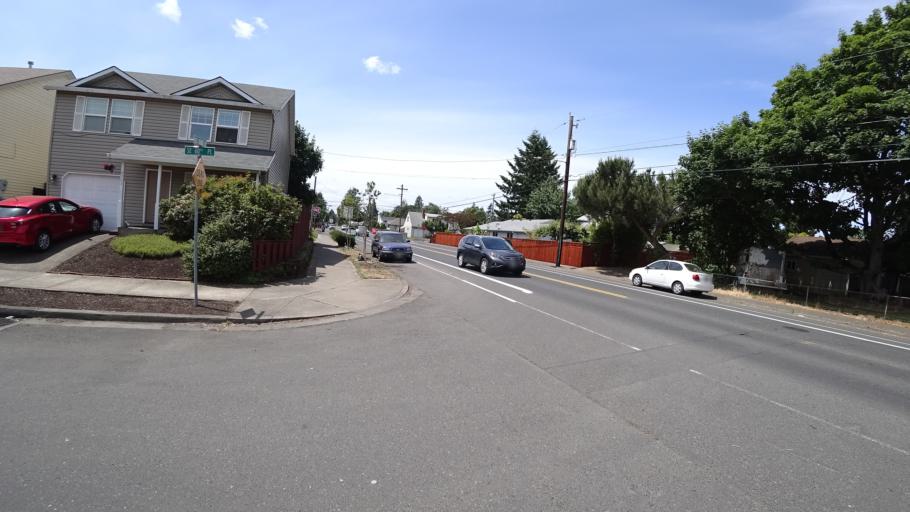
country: US
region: Oregon
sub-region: Multnomah County
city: Lents
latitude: 45.4757
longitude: -122.6013
